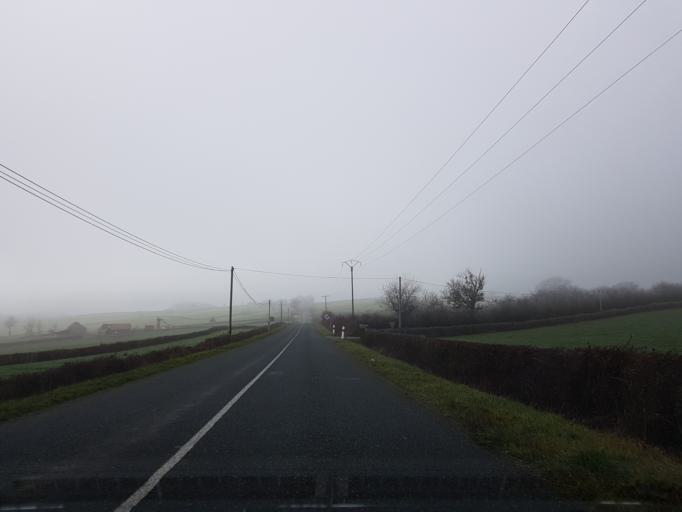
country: FR
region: Bourgogne
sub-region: Departement de Saone-et-Loire
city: Toulon-sur-Arroux
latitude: 46.7048
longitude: 4.2123
